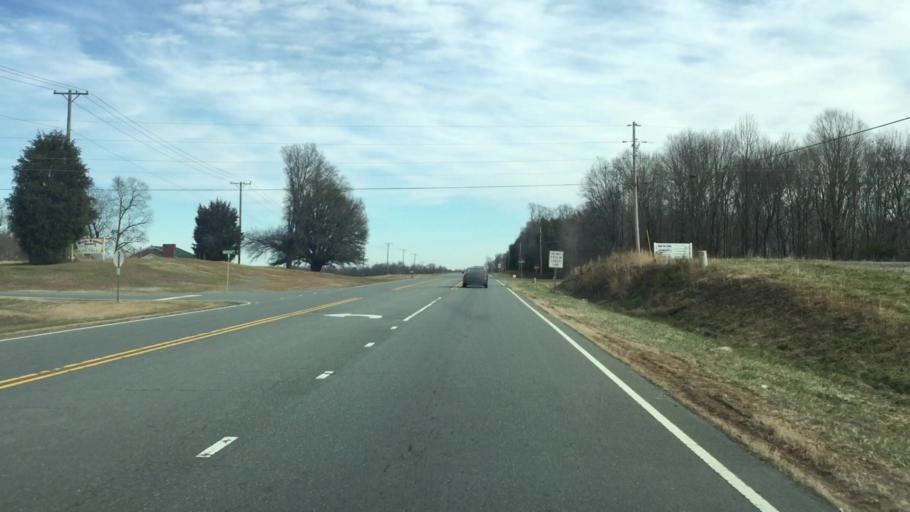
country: US
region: North Carolina
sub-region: Forsyth County
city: Walkertown
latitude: 36.1908
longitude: -80.1034
